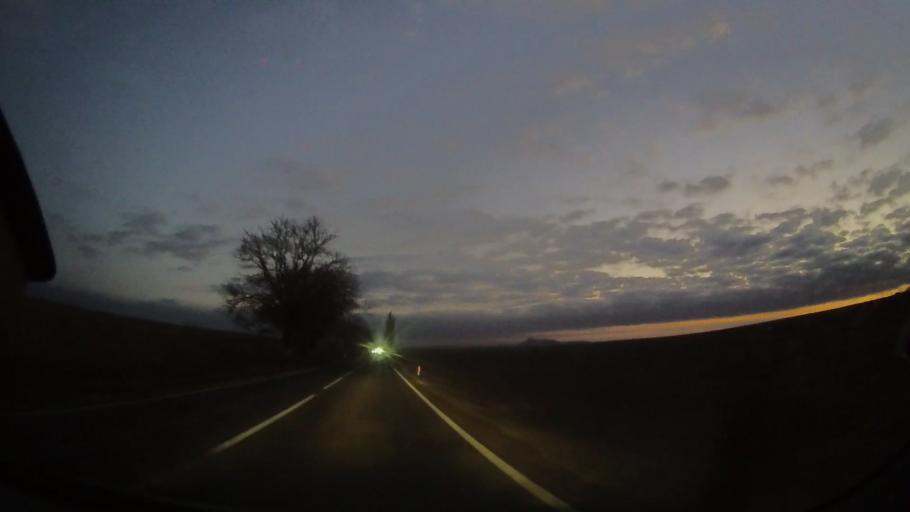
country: RO
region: Tulcea
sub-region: Comuna Frecatei
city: Cataloi
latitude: 45.0898
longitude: 28.7410
